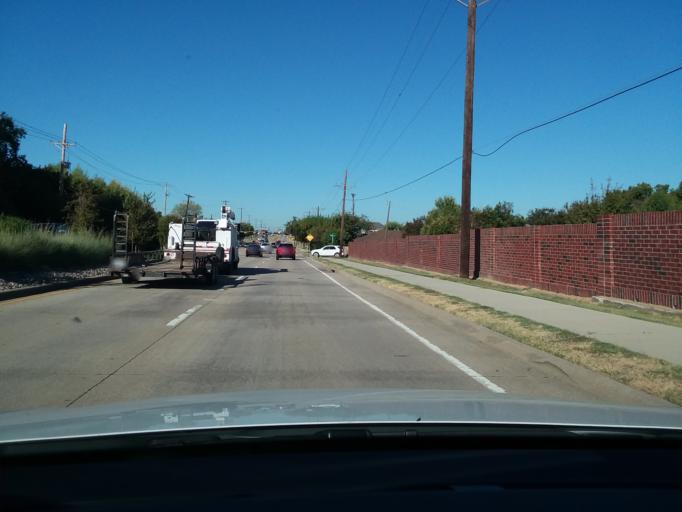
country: US
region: Texas
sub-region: Denton County
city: Highland Village
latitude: 33.0717
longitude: -97.0434
